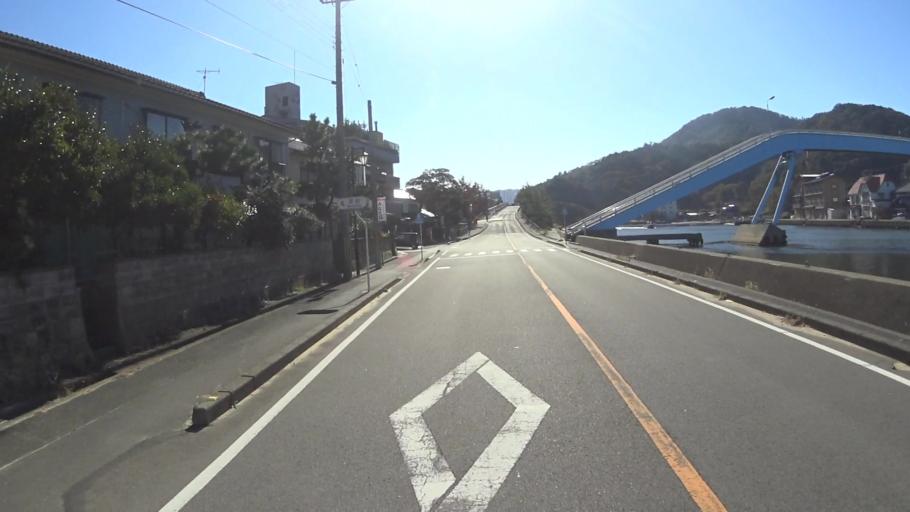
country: JP
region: Hyogo
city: Toyooka
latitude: 35.6446
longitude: 134.9025
